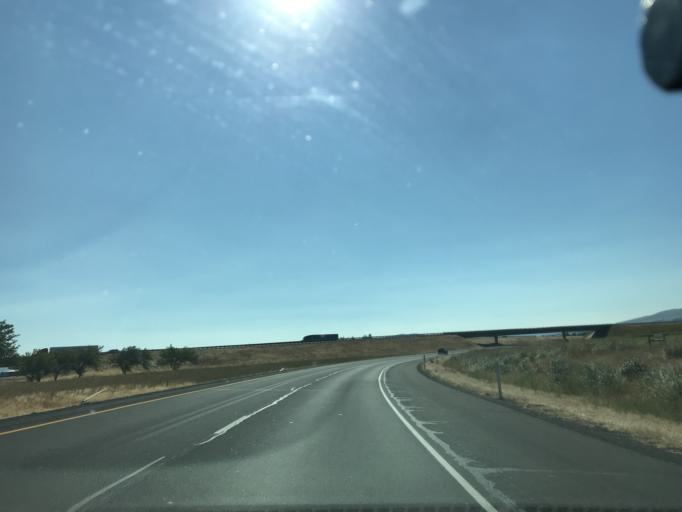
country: US
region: Washington
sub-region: Kittitas County
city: Ellensburg
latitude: 46.9698
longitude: -120.5138
